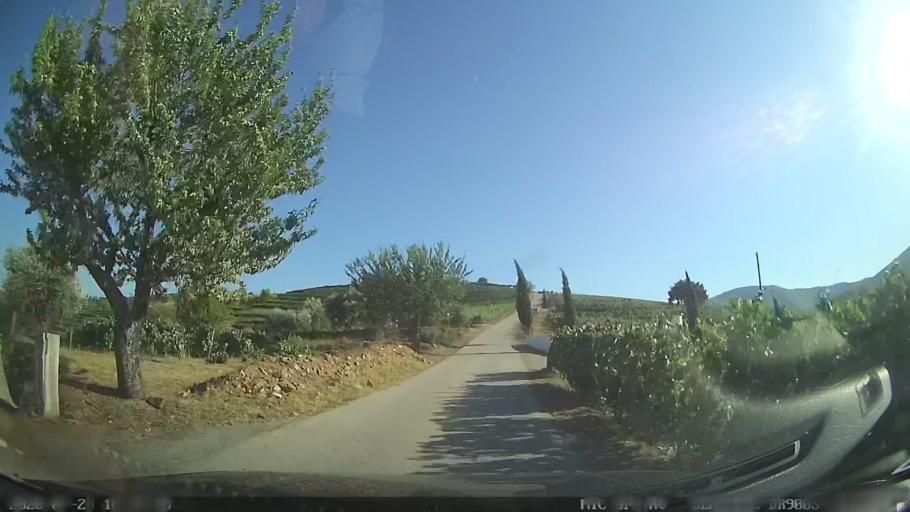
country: PT
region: Viseu
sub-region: Sao Joao da Pesqueira
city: Sao Joao da Pesqueira
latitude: 41.1824
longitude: -7.4025
